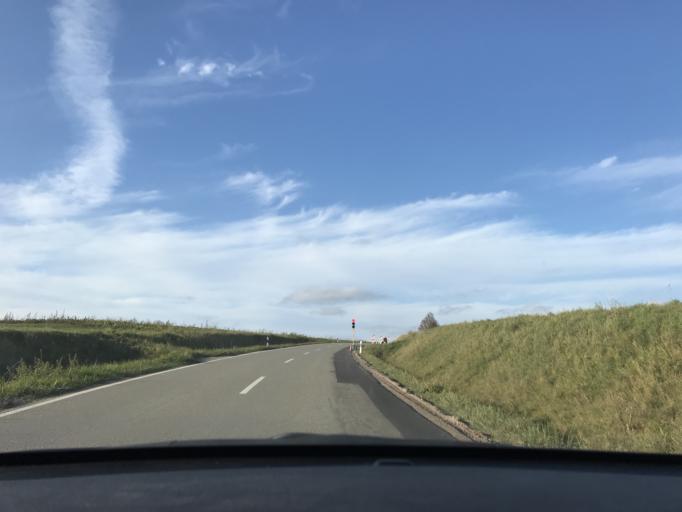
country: DE
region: Bavaria
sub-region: Upper Palatinate
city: Pentling
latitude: 48.9542
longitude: 12.0810
